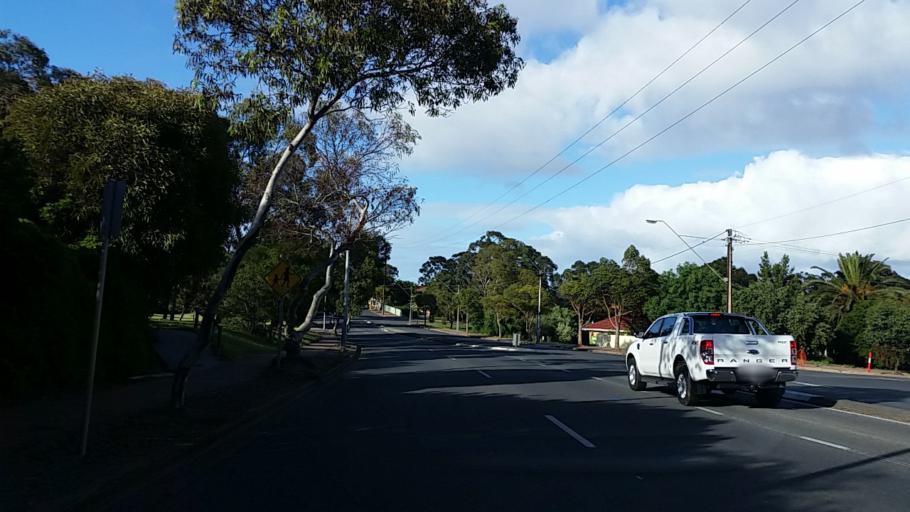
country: AU
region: South Australia
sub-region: Mitcham
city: Clapham
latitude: -35.0021
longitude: 138.5904
